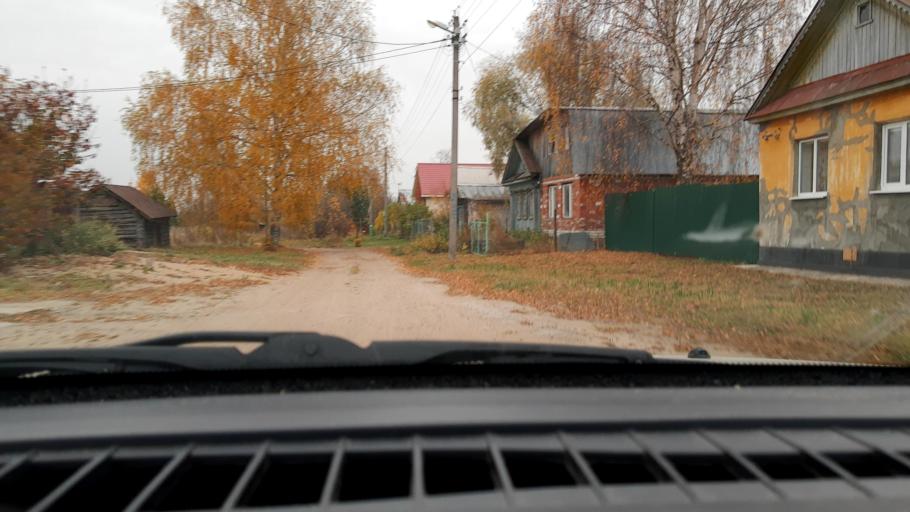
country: RU
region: Nizjnij Novgorod
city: Burevestnik
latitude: 56.0476
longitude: 43.8457
